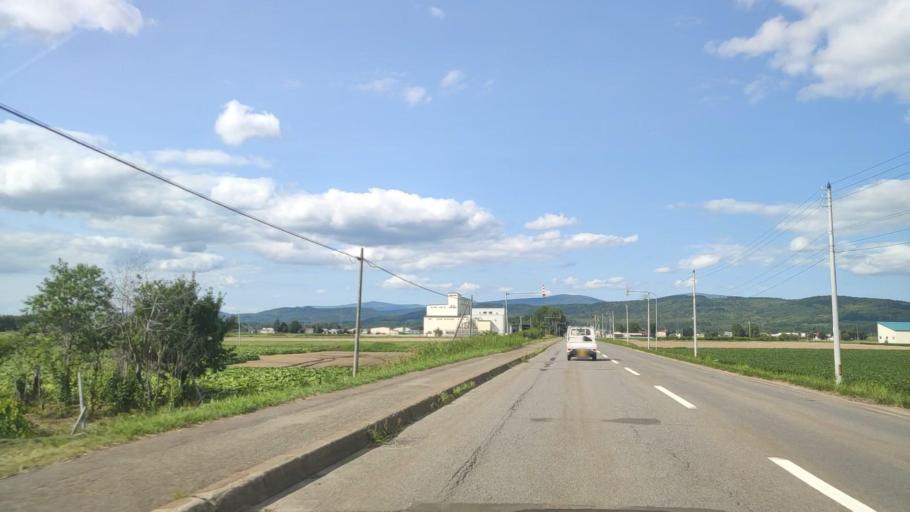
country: JP
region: Hokkaido
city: Nayoro
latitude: 44.4296
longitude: 142.4003
